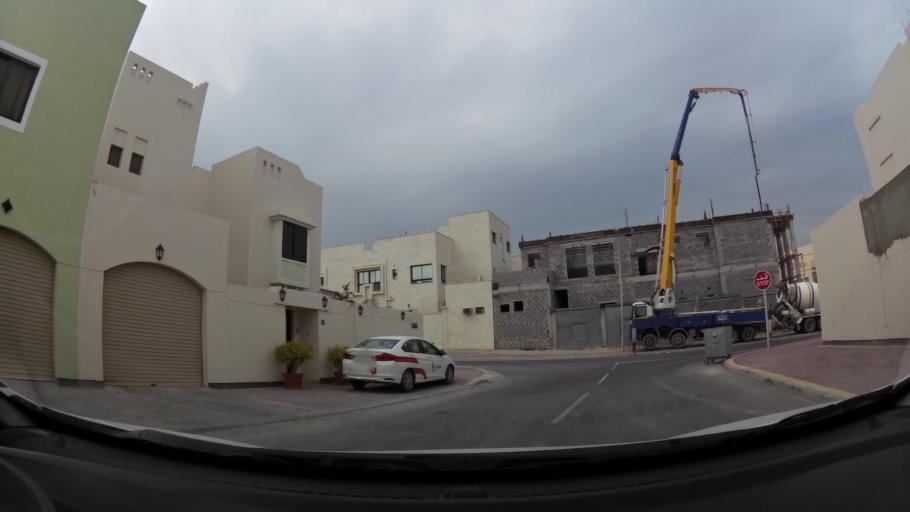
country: BH
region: Northern
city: Ar Rifa'
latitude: 26.0521
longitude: 50.6178
